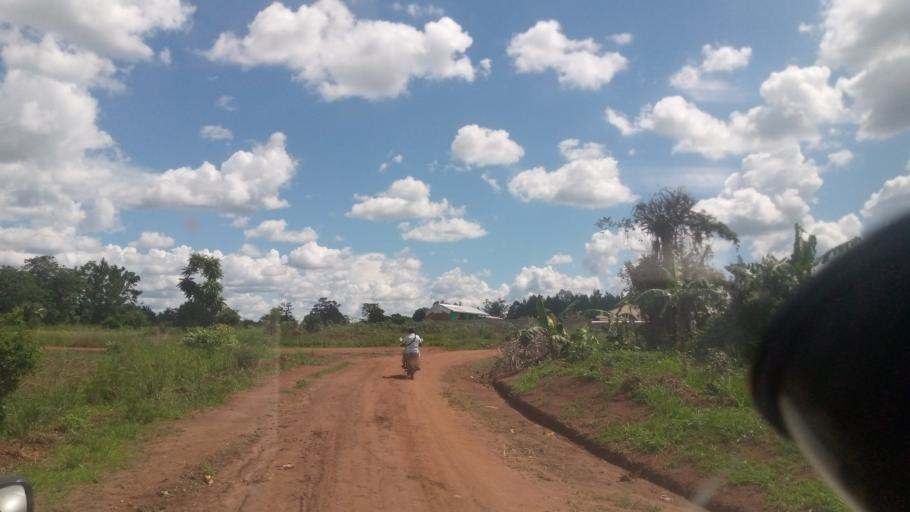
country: UG
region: Northern Region
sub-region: Lira District
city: Lira
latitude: 2.2317
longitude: 32.9071
